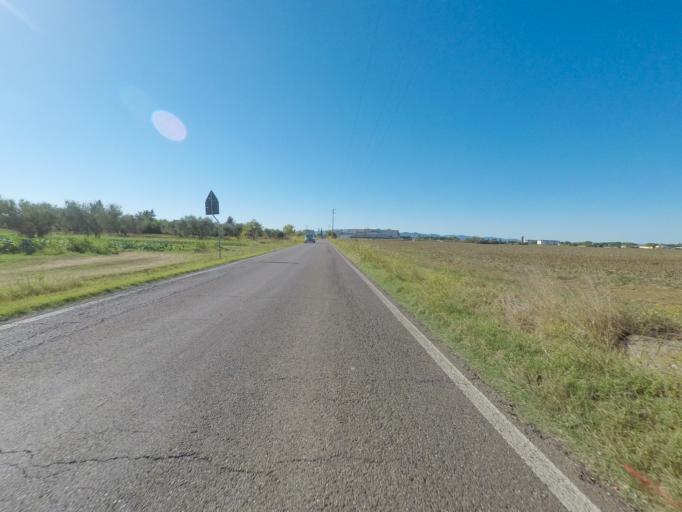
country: IT
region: Tuscany
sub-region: Provincia di Grosseto
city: Grosseto
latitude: 42.7734
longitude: 11.1382
